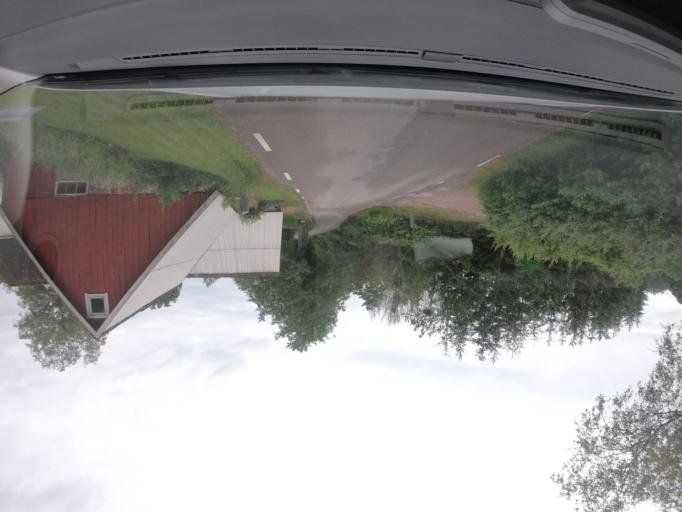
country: SE
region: Skane
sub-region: Orkelljunga Kommun
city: OErkelljunga
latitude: 56.2589
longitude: 13.1705
